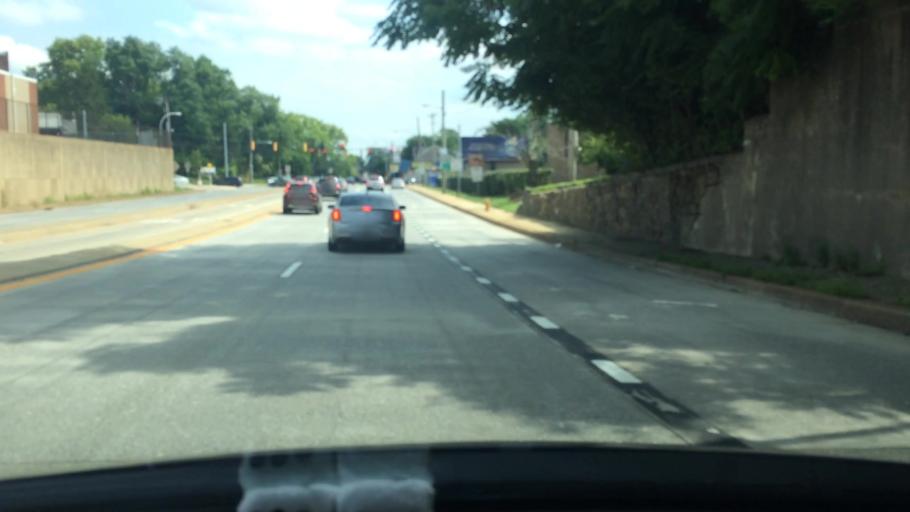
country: US
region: Delaware
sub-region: New Castle County
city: Wilmington
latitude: 39.7647
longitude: -75.5428
